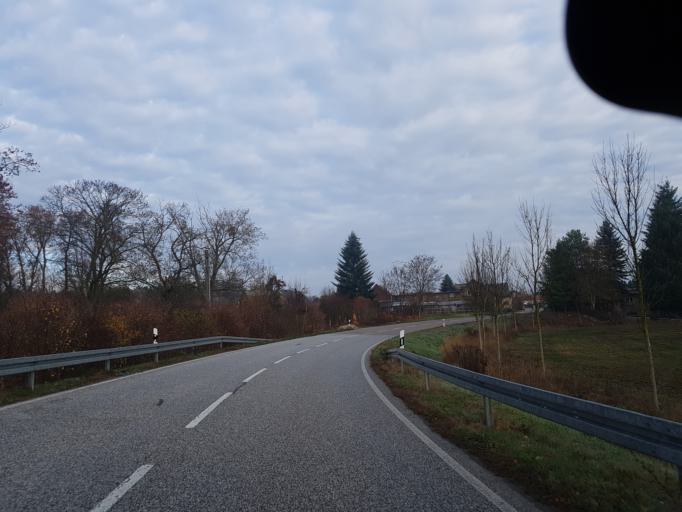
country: DE
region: Saxony-Anhalt
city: Kropstadt
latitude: 51.9351
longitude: 12.7563
